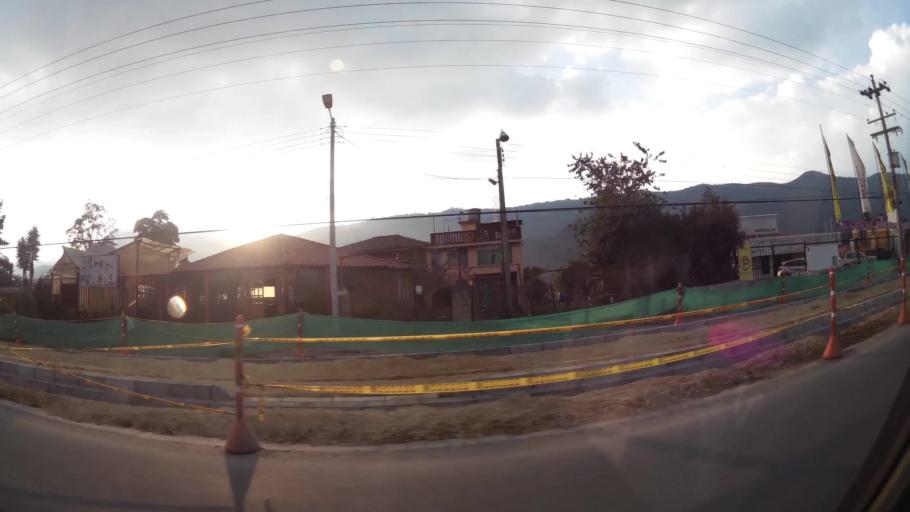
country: CO
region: Cundinamarca
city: Cota
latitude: 4.8234
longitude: -74.0927
